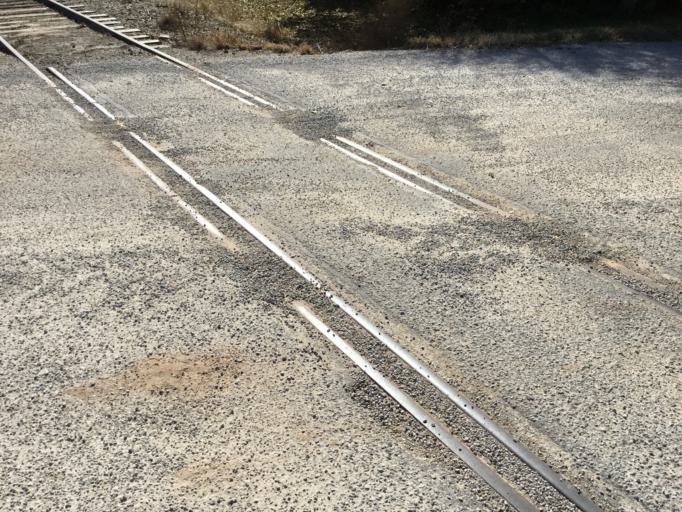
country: US
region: Kansas
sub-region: Lincoln County
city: Lincoln
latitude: 38.9293
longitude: -98.0110
